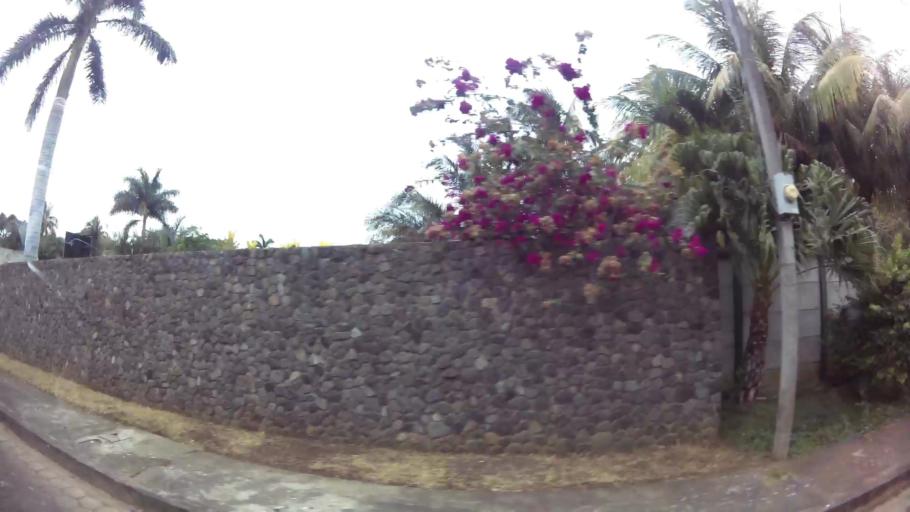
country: NI
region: Managua
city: Managua
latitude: 12.0903
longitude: -86.2275
